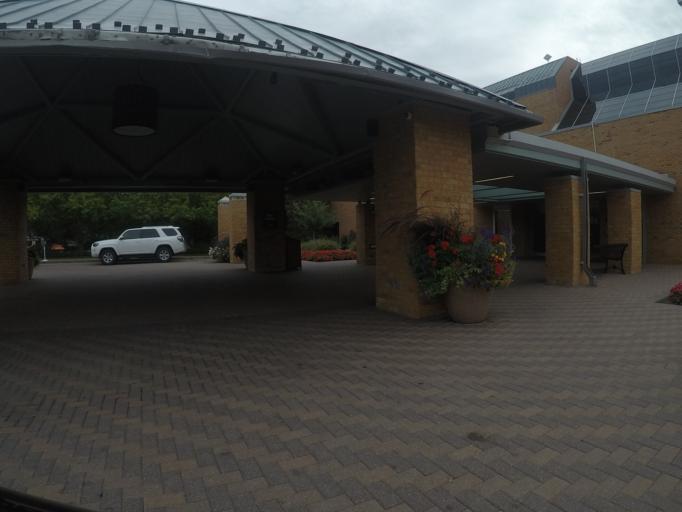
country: US
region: Colorado
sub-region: Arapahoe County
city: Centennial
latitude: 39.5704
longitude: -104.8676
